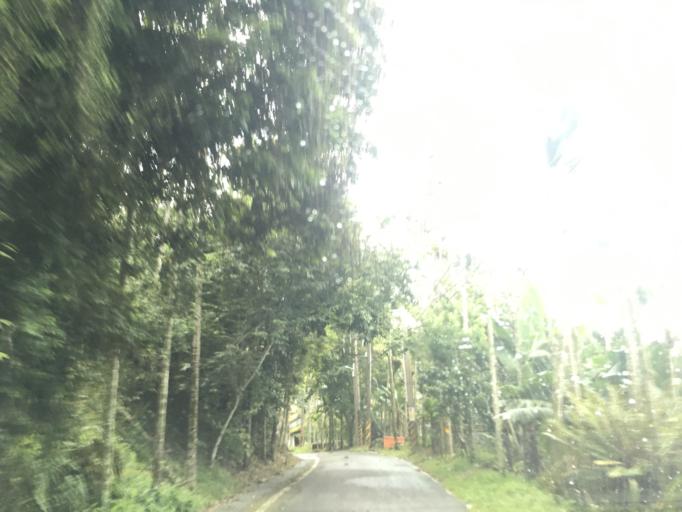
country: TW
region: Taiwan
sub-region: Yunlin
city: Douliu
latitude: 23.5636
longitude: 120.6238
